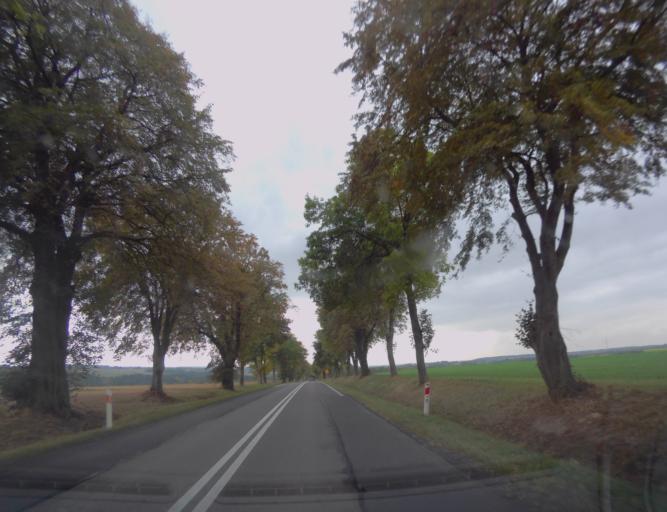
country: PL
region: Lublin Voivodeship
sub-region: Powiat krasnostawski
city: Zolkiewka
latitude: 50.9211
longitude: 22.8775
